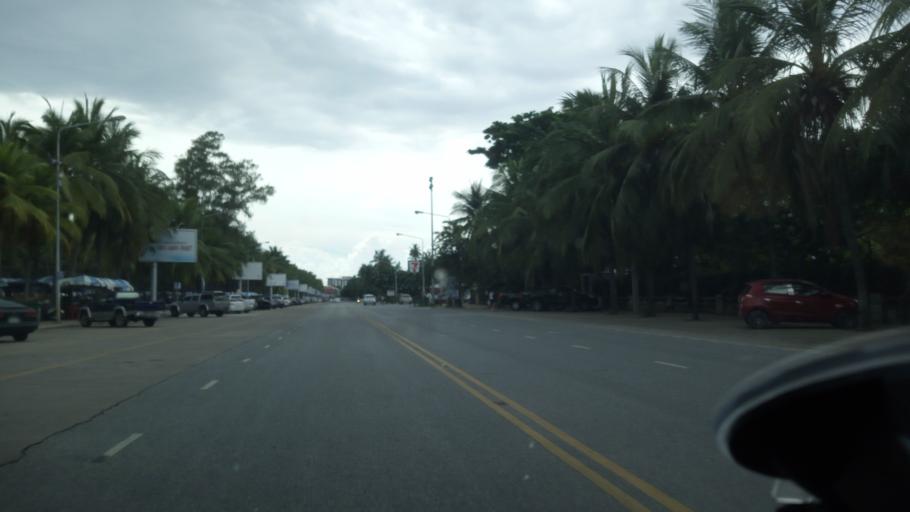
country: TH
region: Chon Buri
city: Chon Buri
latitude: 13.2943
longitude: 100.9067
